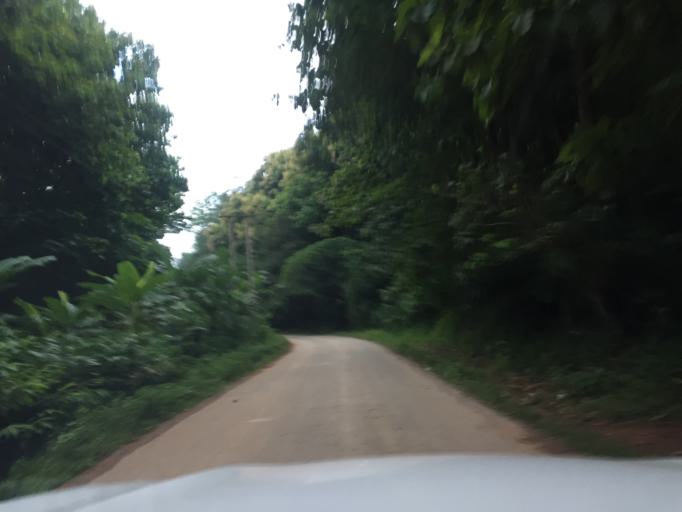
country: LA
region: Phongsali
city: Khoa
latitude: 21.0806
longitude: 102.3731
